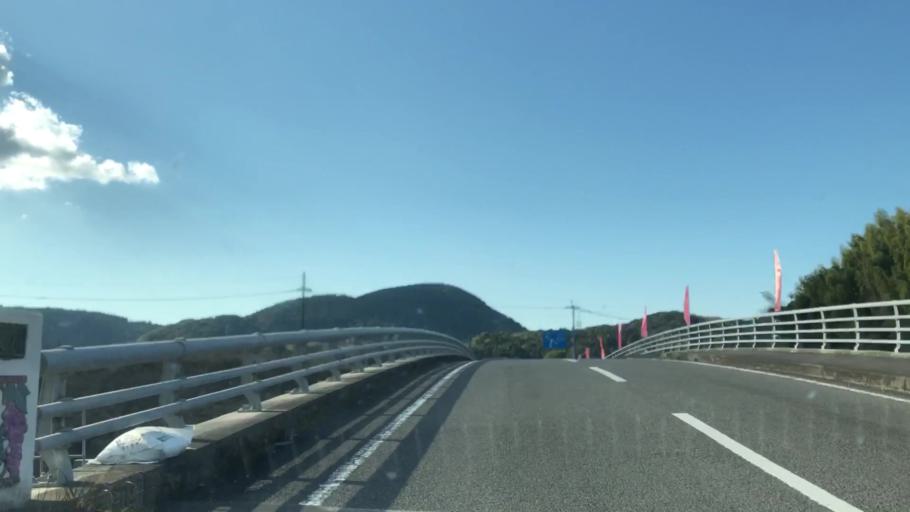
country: JP
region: Kagoshima
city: Satsumasendai
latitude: 31.8647
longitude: 130.3308
